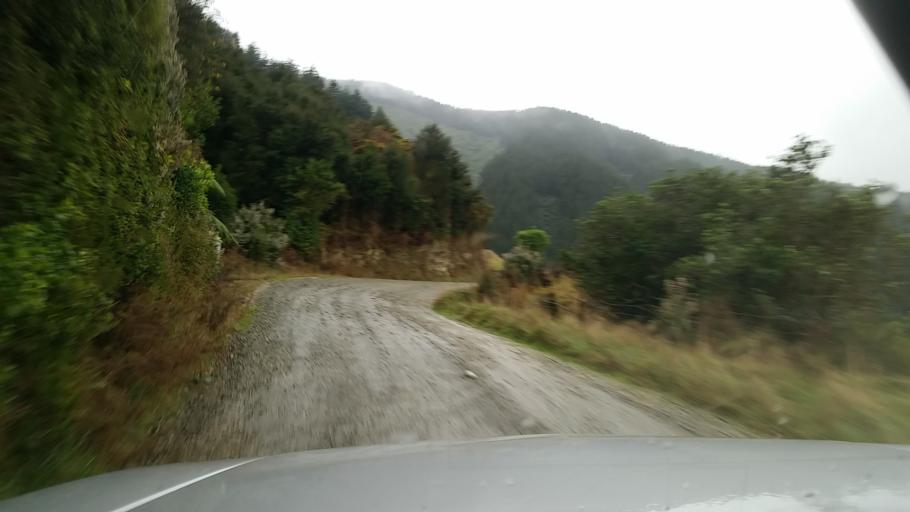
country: NZ
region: Marlborough
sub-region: Marlborough District
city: Picton
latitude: -41.1455
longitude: 174.0509
